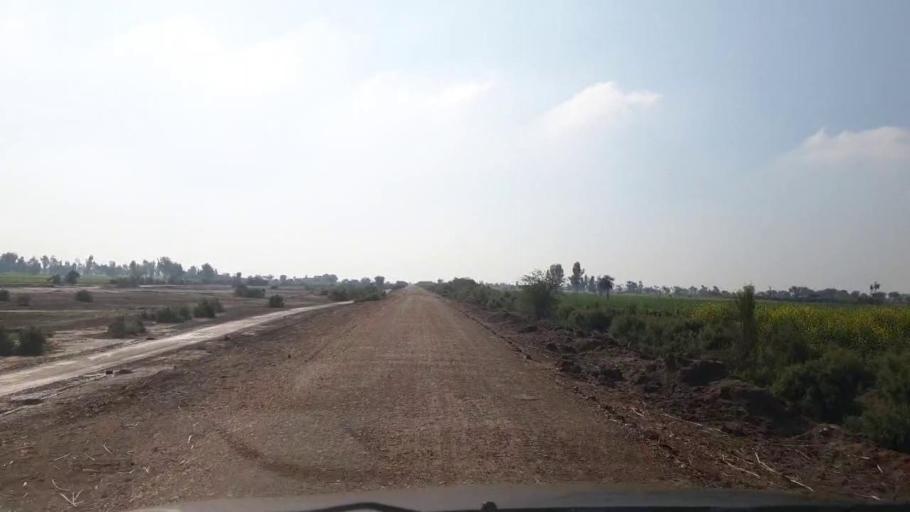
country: PK
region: Sindh
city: Sinjhoro
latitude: 26.0463
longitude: 68.7783
